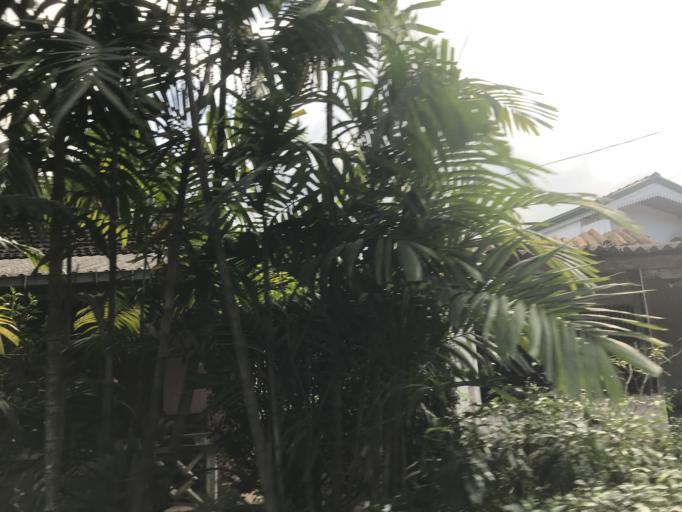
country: LK
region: Western
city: Gampaha
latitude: 7.0779
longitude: 79.9902
